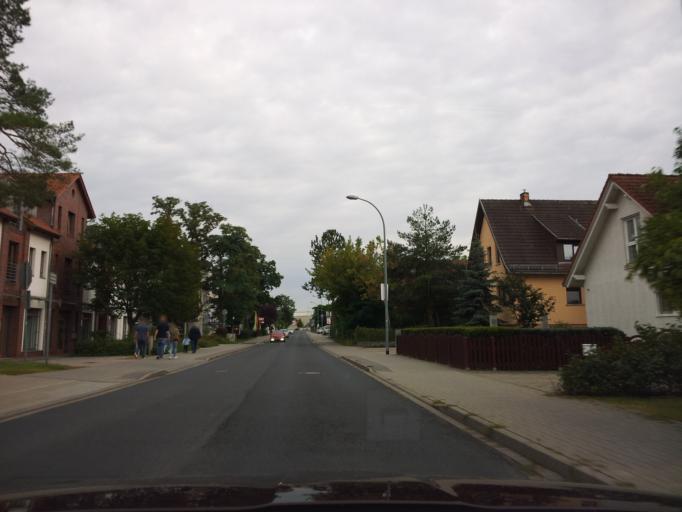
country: DE
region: Brandenburg
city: Ludwigsfelde
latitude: 52.3068
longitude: 13.2584
